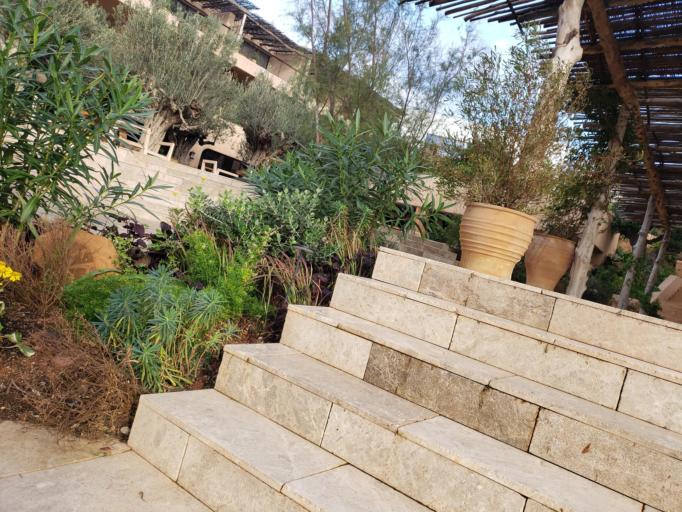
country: ES
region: Balearic Islands
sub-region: Illes Balears
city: Sant Joan de Labritja
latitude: 39.1109
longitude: 1.5074
